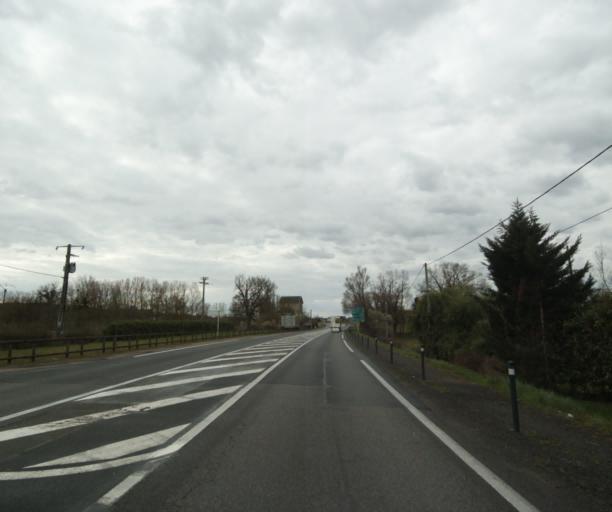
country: FR
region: Auvergne
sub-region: Departement de l'Allier
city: Toulon-sur-Allier
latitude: 46.5003
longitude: 3.3635
